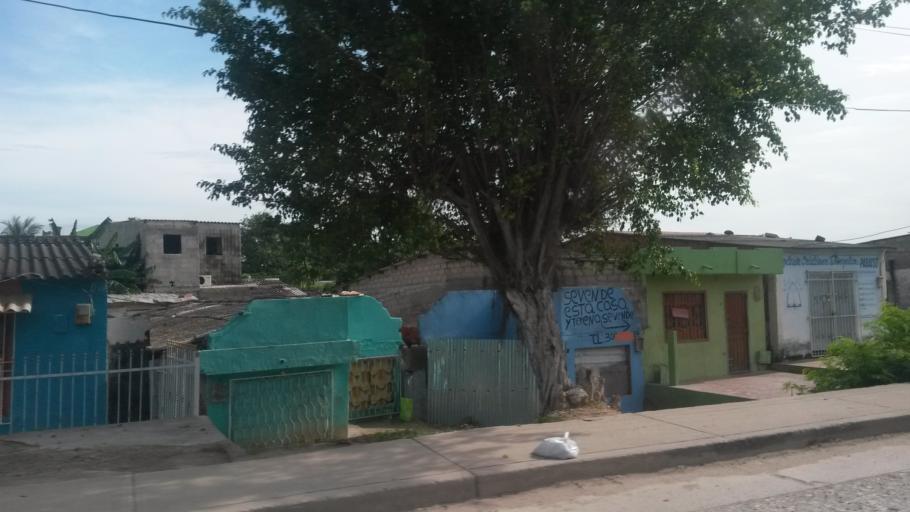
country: CO
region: Bolivar
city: Cartagena
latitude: 10.4033
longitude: -75.4758
